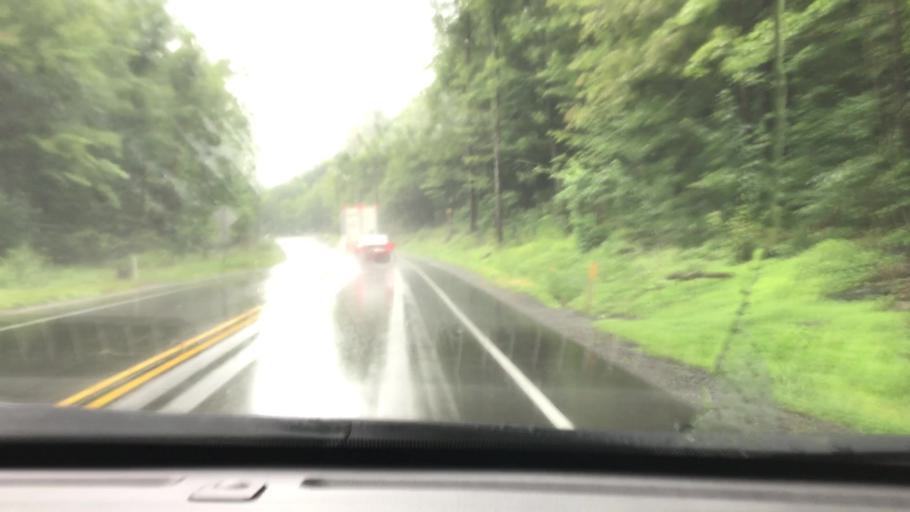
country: US
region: Pennsylvania
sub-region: Clearfield County
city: Osceola Mills
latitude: 40.7646
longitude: -78.2352
